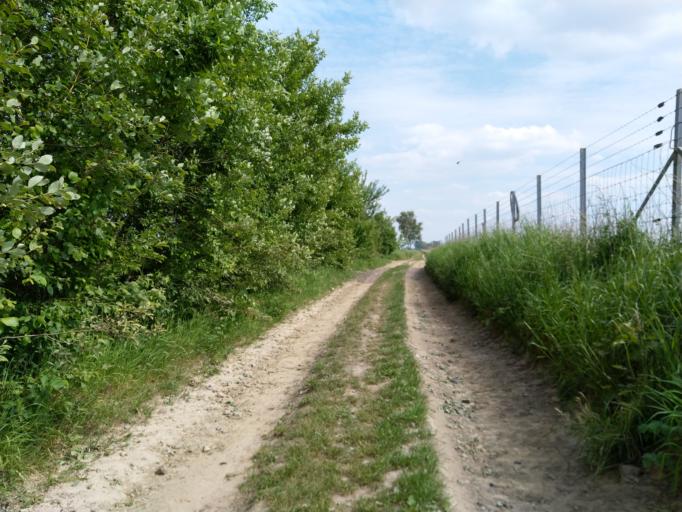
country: BE
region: Wallonia
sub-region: Province du Hainaut
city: Jurbise
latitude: 50.5501
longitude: 3.9298
